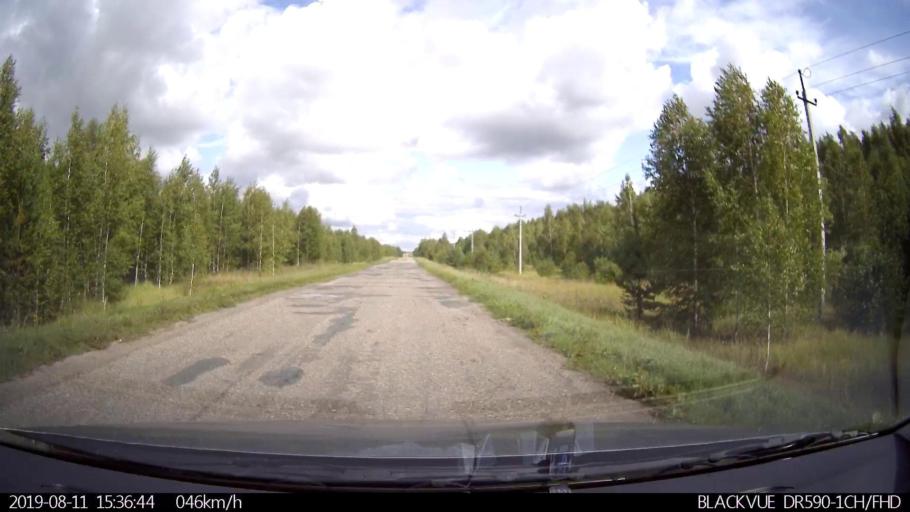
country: RU
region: Ulyanovsk
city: Ignatovka
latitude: 53.8592
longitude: 47.6239
